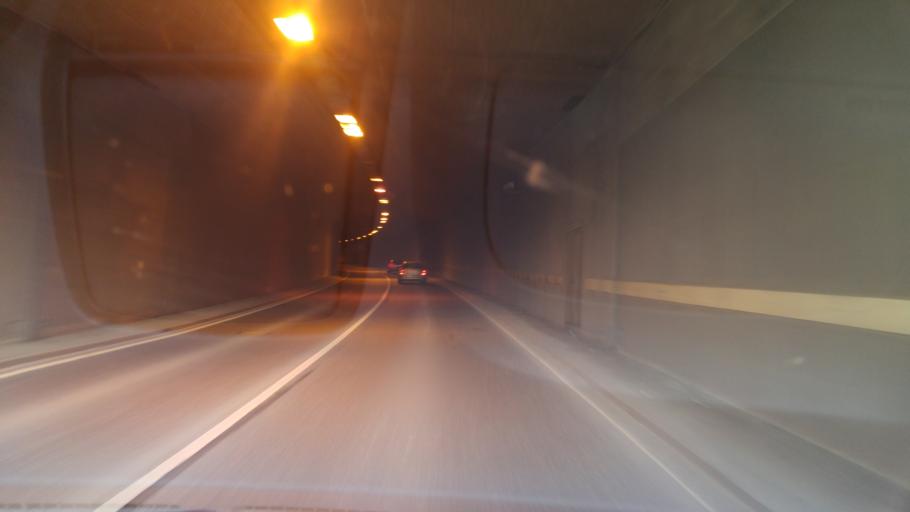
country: DE
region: Baden-Wuerttemberg
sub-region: Regierungsbezirk Stuttgart
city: Ditzingen
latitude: 48.8218
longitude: 9.0551
